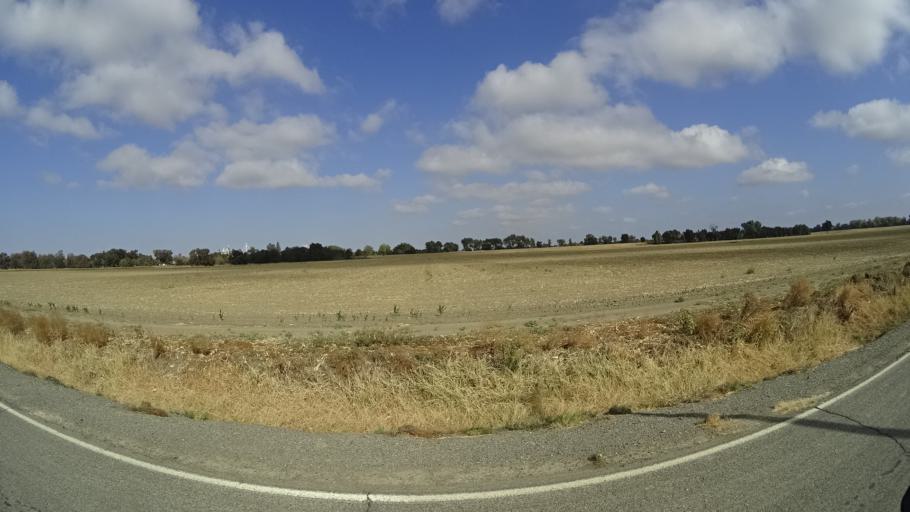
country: US
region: California
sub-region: Yolo County
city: Woodland
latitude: 38.7956
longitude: -121.7121
